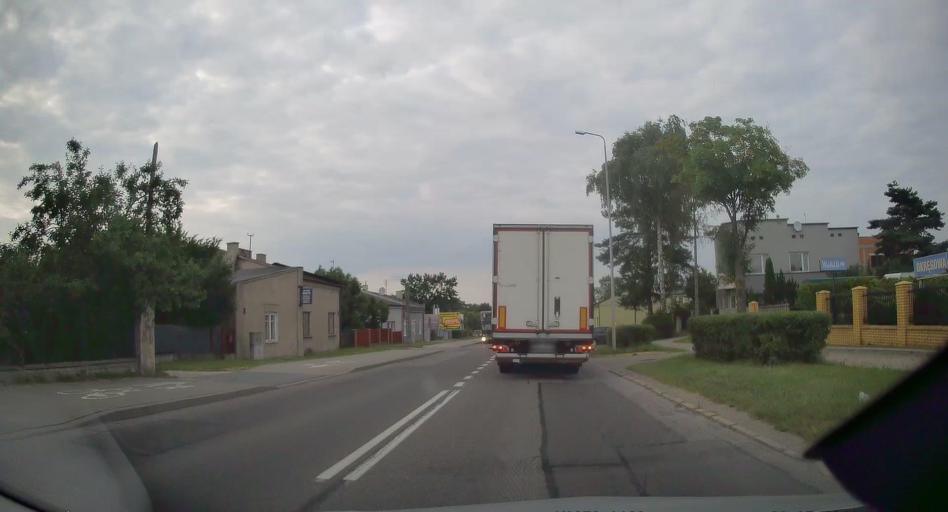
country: PL
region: Lodz Voivodeship
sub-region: Powiat radomszczanski
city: Radomsko
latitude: 51.0561
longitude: 19.4407
